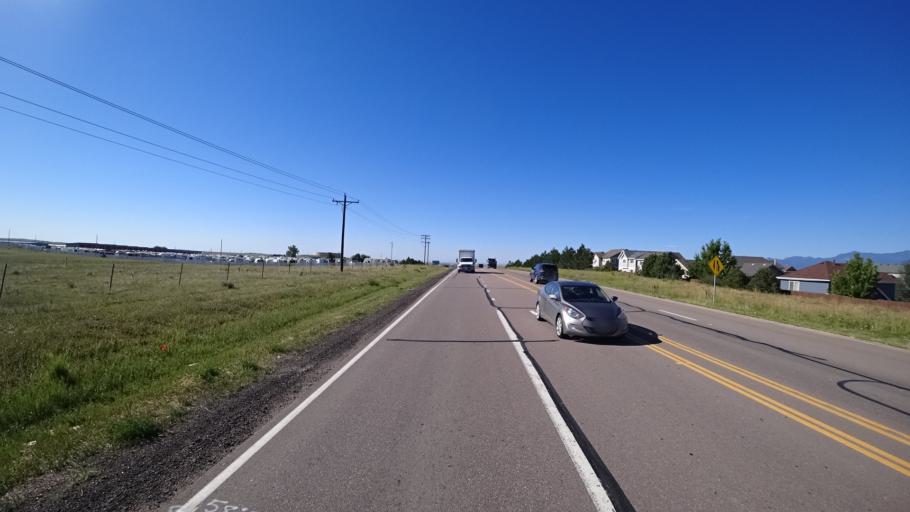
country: US
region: Colorado
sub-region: El Paso County
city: Cimarron Hills
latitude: 38.9097
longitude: -104.6828
